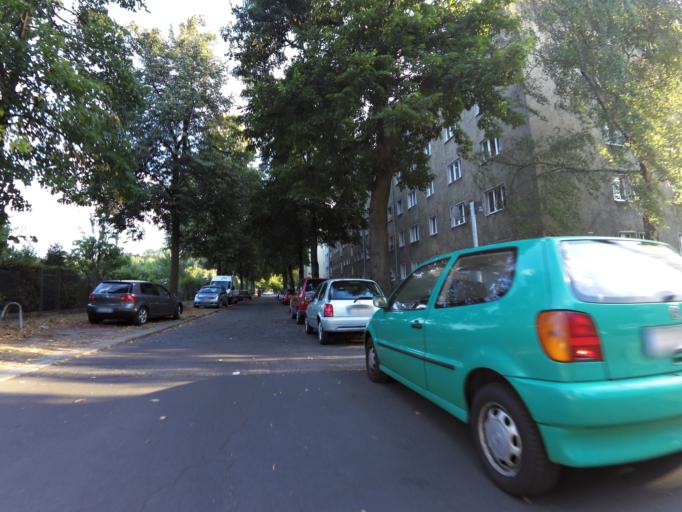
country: DE
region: Berlin
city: Schoneberg Bezirk
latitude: 52.4611
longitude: 13.3502
